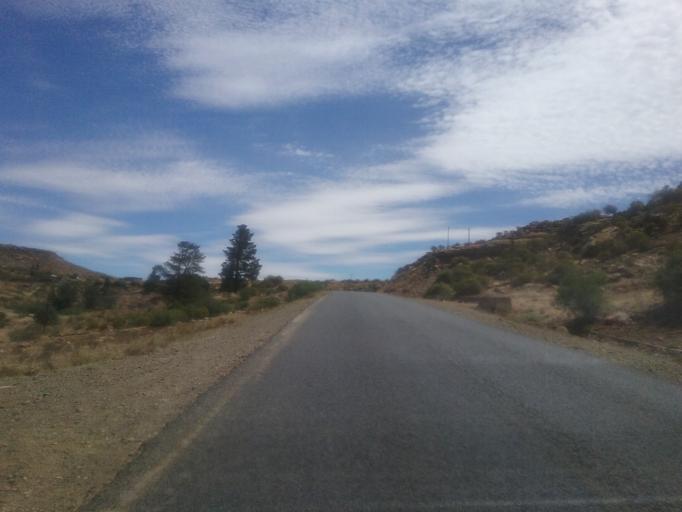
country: LS
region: Mohale's Hoek District
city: Mohale's Hoek
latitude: -30.0802
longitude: 27.4279
